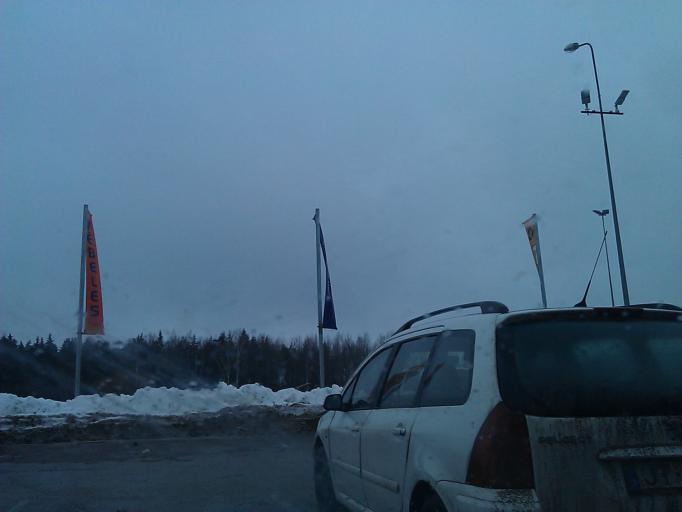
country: LV
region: Cesu Rajons
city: Cesis
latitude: 57.2965
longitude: 25.3027
